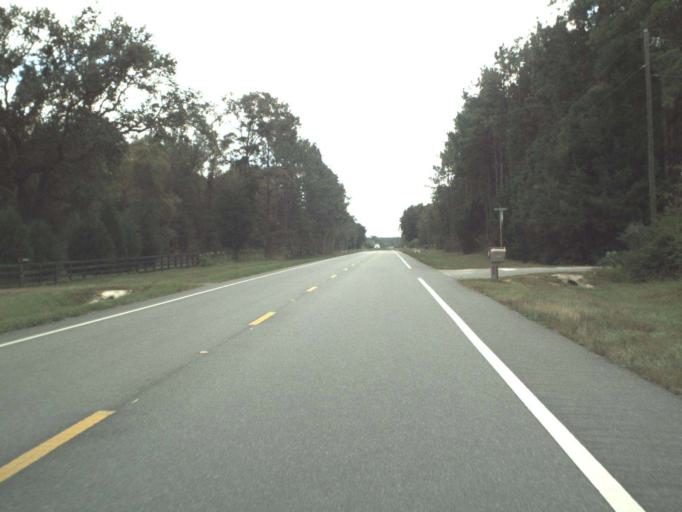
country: US
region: Florida
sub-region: Calhoun County
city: Blountstown
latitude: 30.3723
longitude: -85.2149
